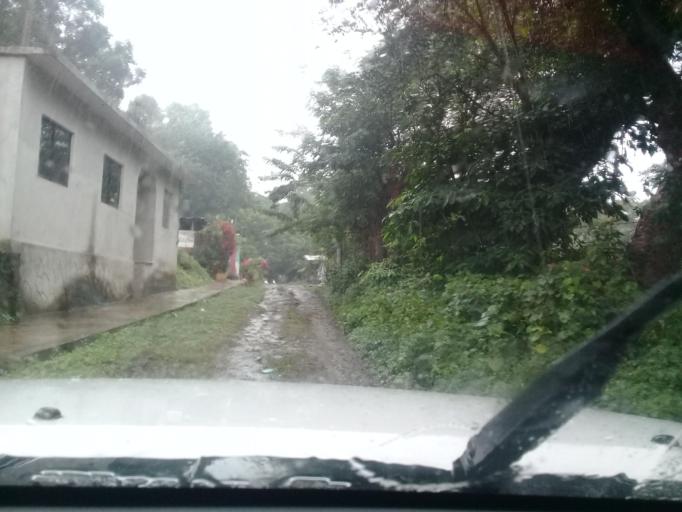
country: MX
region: Veracruz
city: Santiago Tuxtla
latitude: 18.4773
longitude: -95.2953
